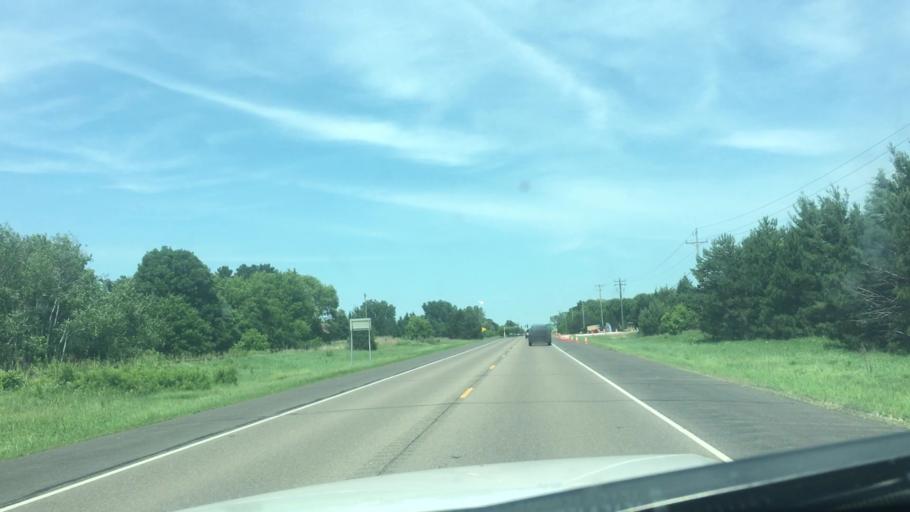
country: US
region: Minnesota
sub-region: Washington County
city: Hugo
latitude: 45.1331
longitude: -93.0011
